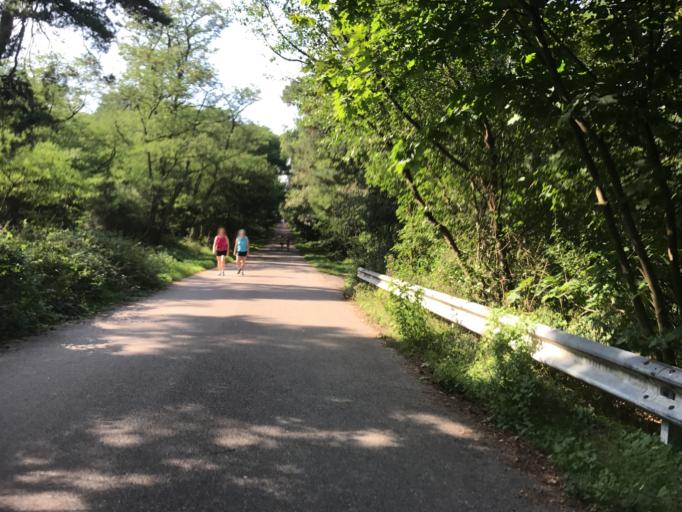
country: DE
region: Rheinland-Pfalz
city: Budenheim
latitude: 50.0088
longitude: 8.1957
